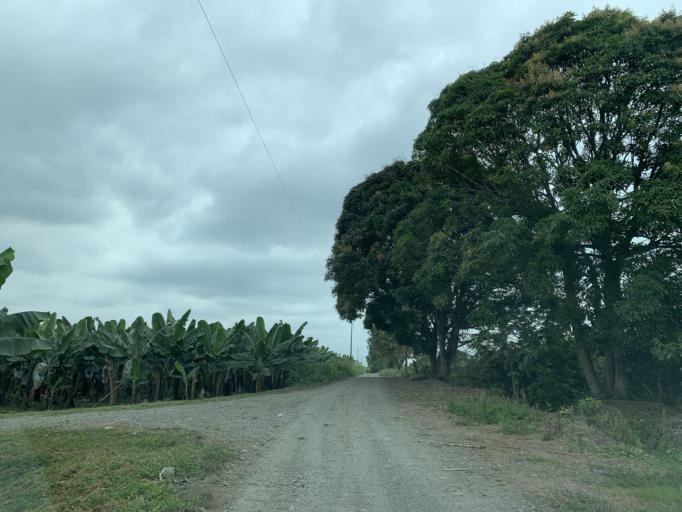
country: EC
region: Guayas
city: Coronel Marcelino Mariduena
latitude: -2.3415
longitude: -79.4577
